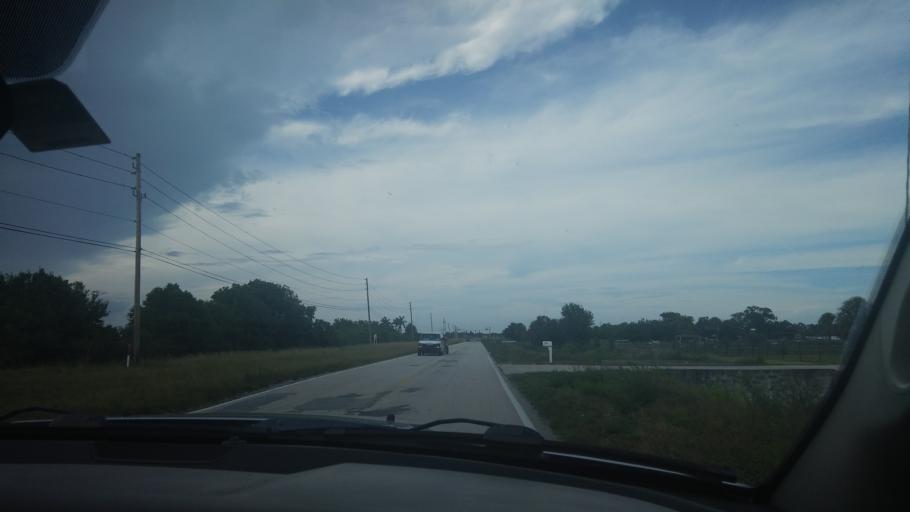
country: US
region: Florida
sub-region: Brevard County
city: Grant-Valkaria
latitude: 27.8929
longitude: -80.6223
